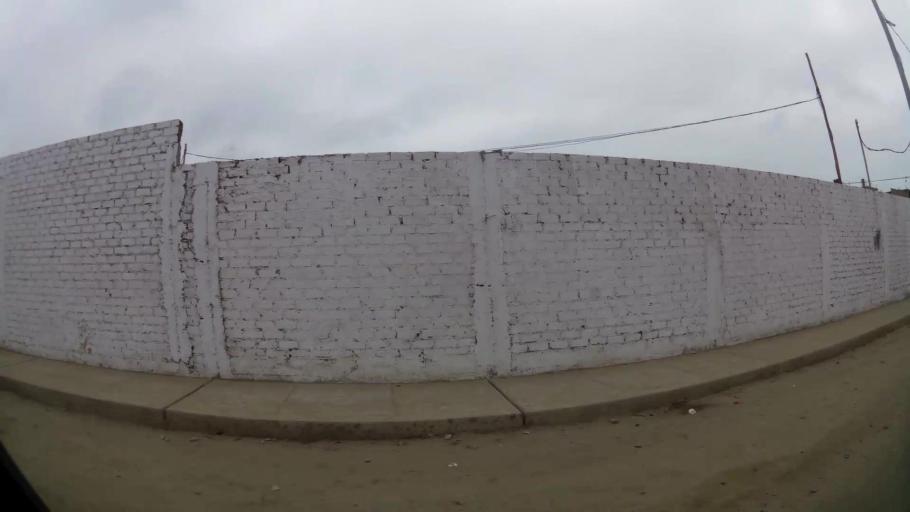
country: PE
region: La Libertad
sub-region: Provincia de Trujillo
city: Trujillo
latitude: -8.1215
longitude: -79.0461
